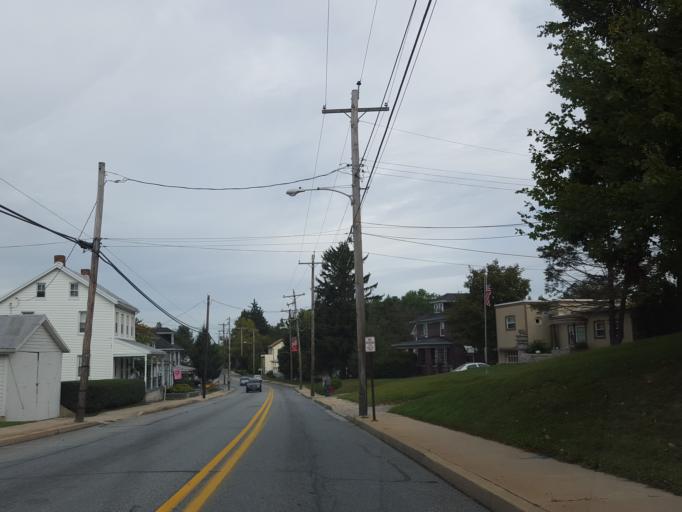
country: US
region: Pennsylvania
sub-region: York County
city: West York
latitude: 39.9023
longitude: -76.7893
